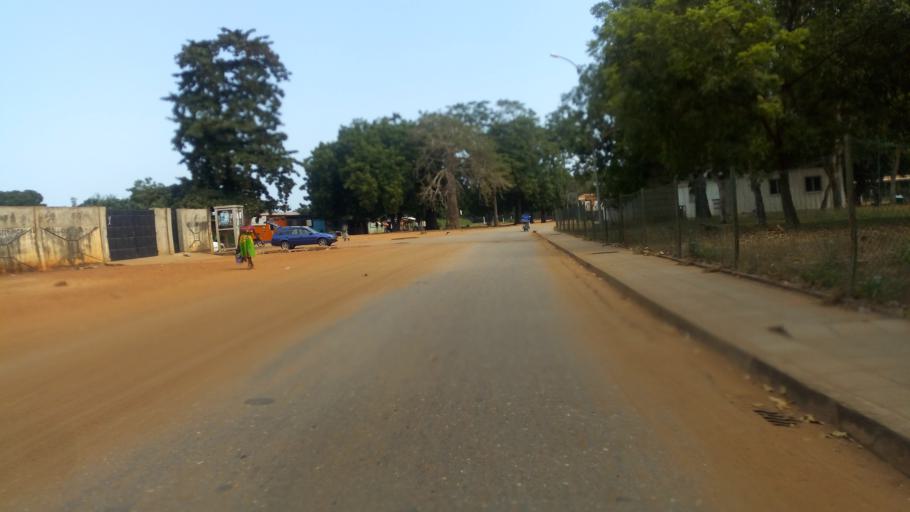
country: TG
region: Maritime
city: Lome
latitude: 6.1800
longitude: 1.2132
